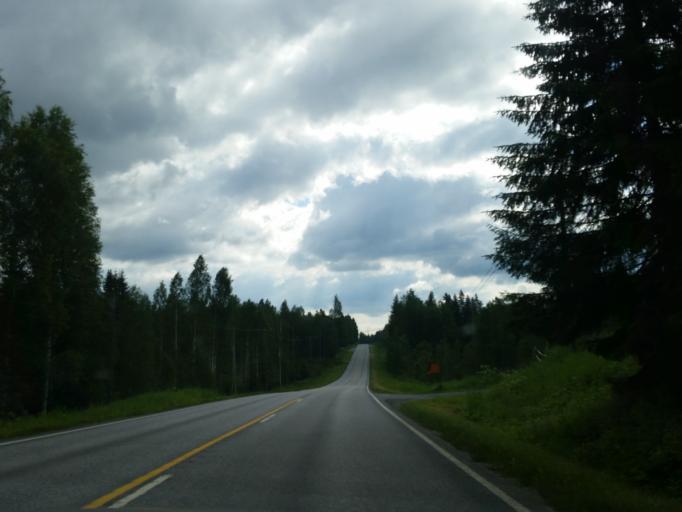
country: FI
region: Northern Savo
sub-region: Kuopio
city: Kuopio
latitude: 62.8455
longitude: 27.4614
